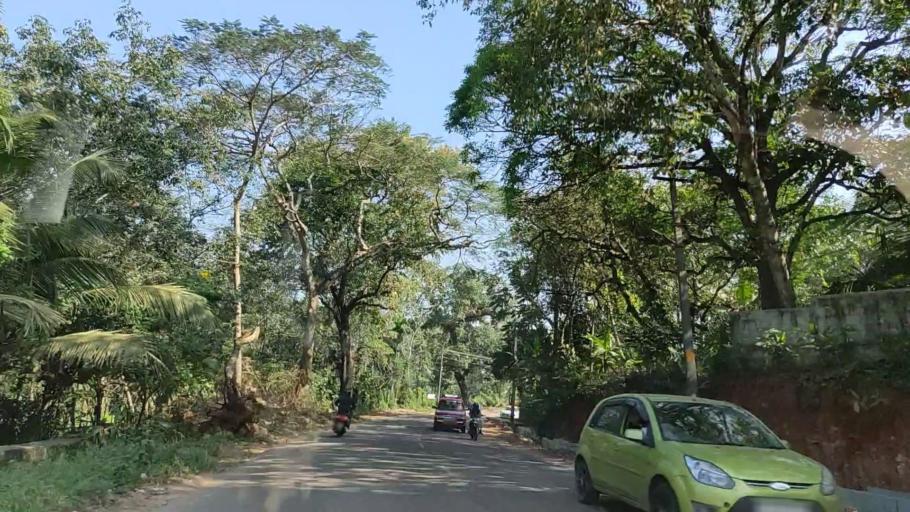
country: IN
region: Kerala
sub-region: Kollam
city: Punalur
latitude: 8.9019
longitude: 76.8666
